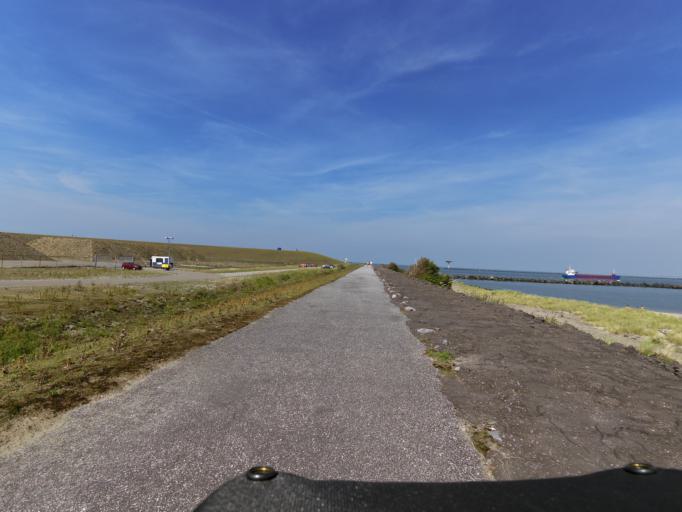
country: NL
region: South Holland
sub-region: Gemeente Rotterdam
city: Hoek van Holland
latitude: 51.9843
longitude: 4.0364
